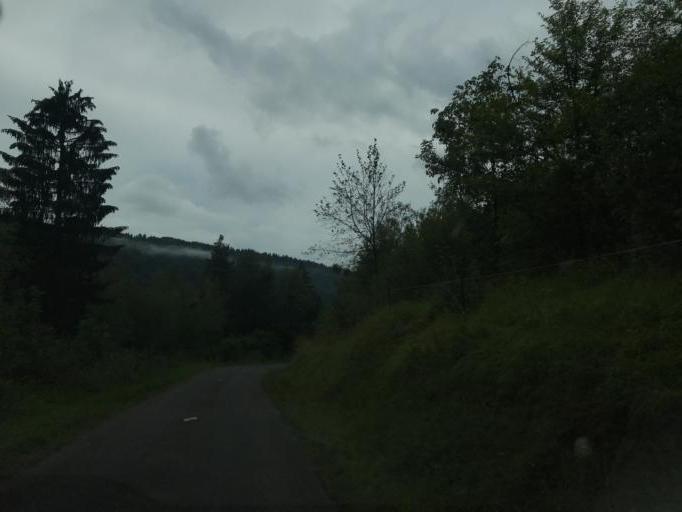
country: FR
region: Franche-Comte
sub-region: Departement du Jura
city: Lavans-les-Saint-Claude
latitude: 46.3207
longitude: 5.7536
